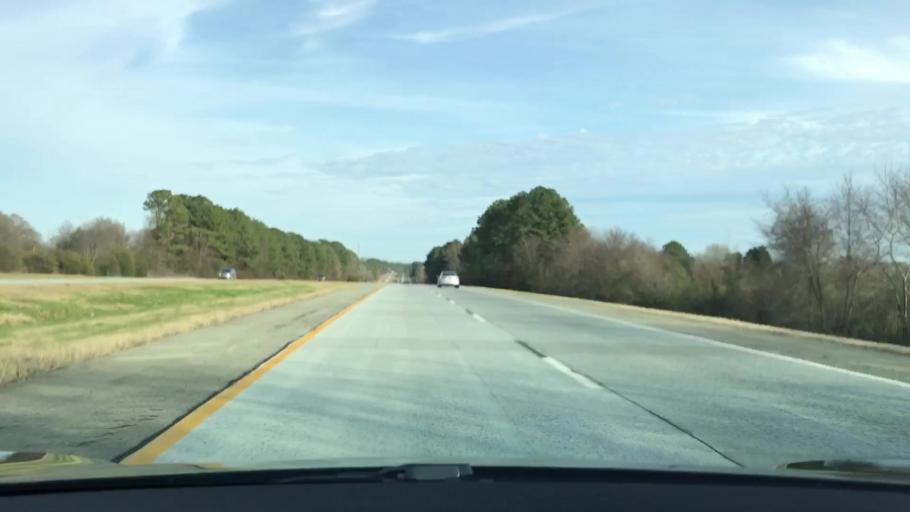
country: US
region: Georgia
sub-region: Morgan County
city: Madison
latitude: 33.5537
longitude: -83.4025
